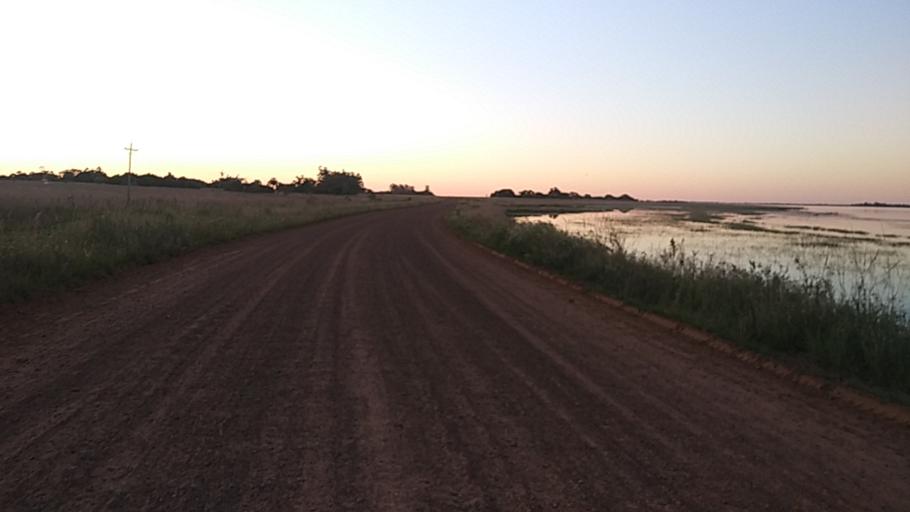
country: AR
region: Corrientes
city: Yataity Calle
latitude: -29.0122
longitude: -58.9106
